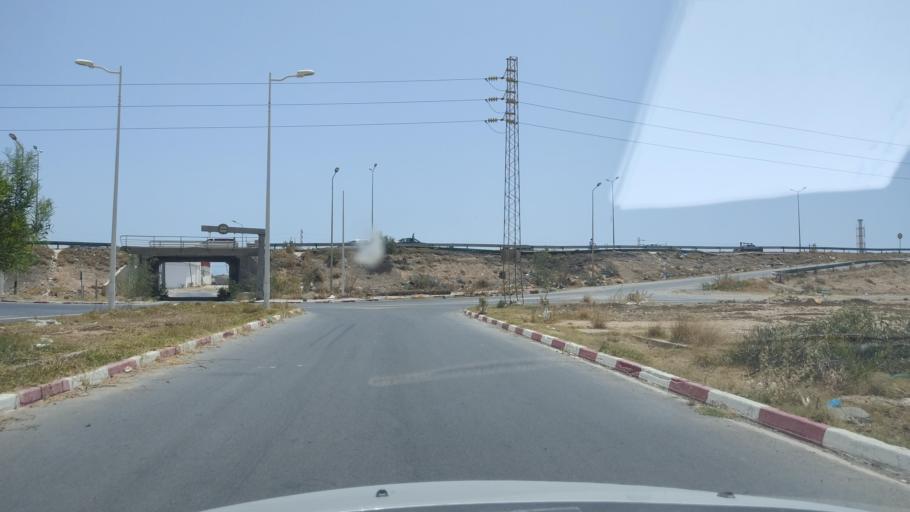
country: TN
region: Safaqis
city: Sfax
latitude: 34.7077
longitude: 10.7214
